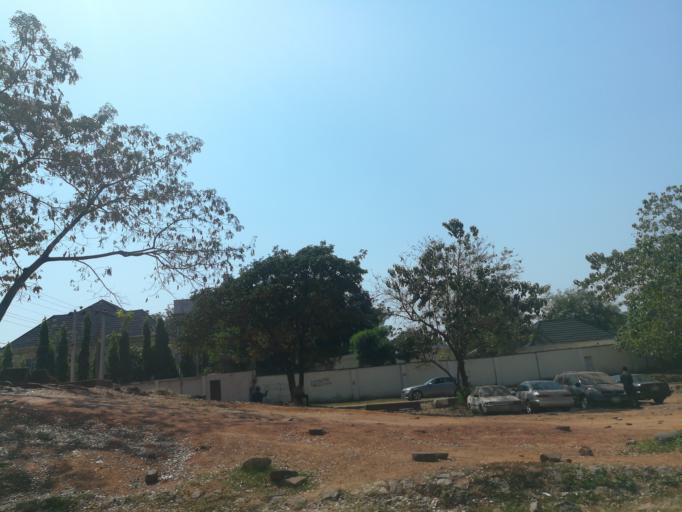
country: NG
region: Abuja Federal Capital Territory
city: Abuja
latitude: 9.0546
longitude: 7.4552
